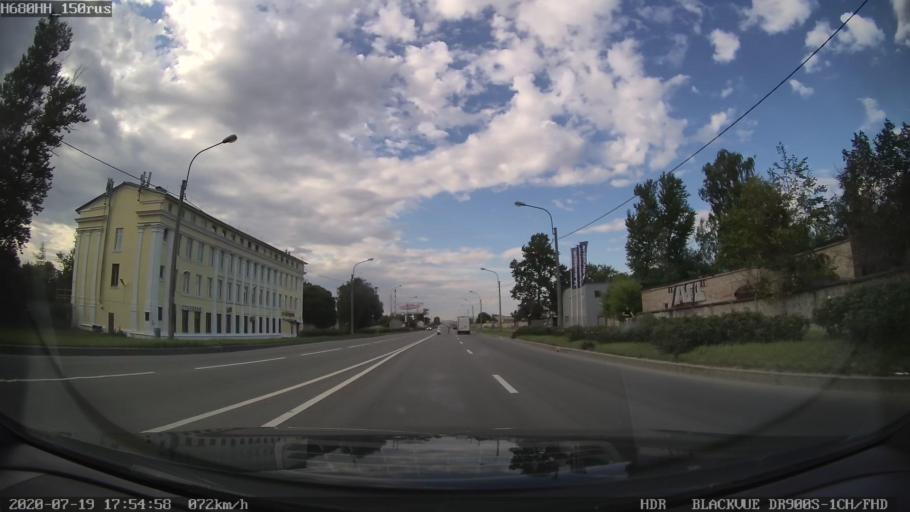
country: RU
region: St.-Petersburg
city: Admiralteisky
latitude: 59.8900
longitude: 30.3024
